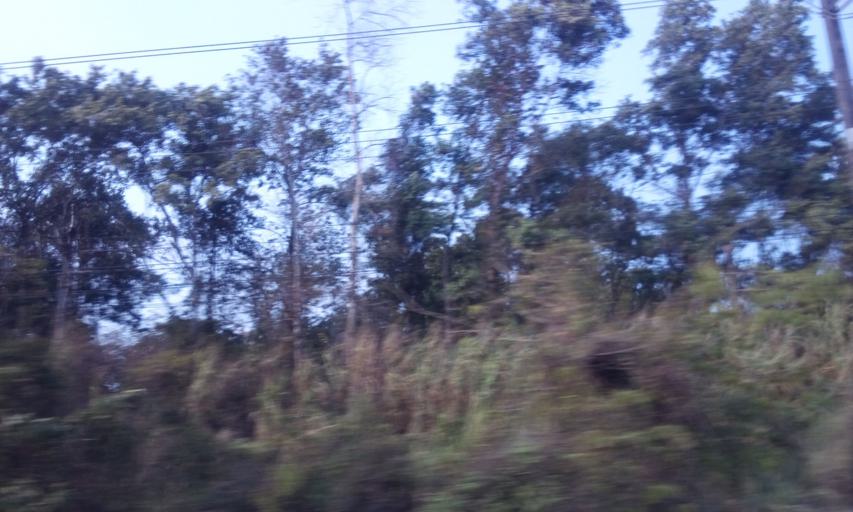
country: TH
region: Chanthaburi
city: Khlung
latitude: 12.4541
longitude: 102.2797
